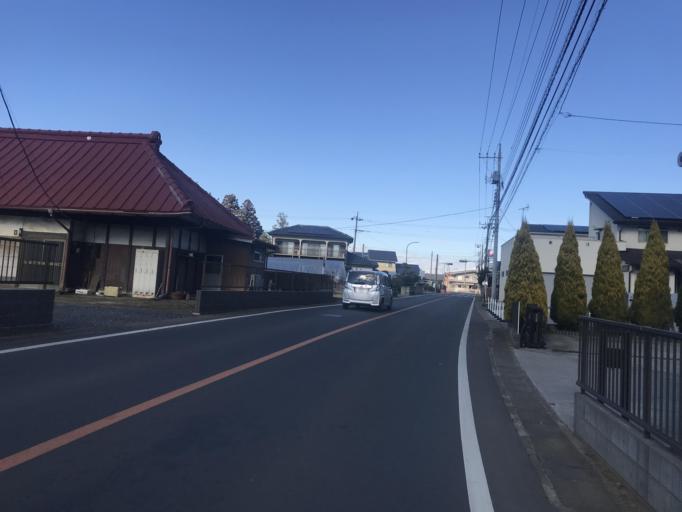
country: JP
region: Tochigi
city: Kaminokawa
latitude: 36.4039
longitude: 139.8772
